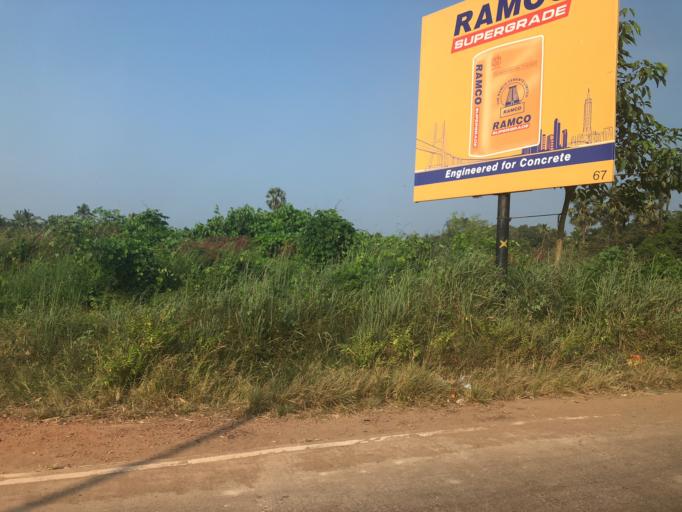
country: IN
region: Karnataka
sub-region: Dakshina Kannada
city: Ullal
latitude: 12.8159
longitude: 74.8503
